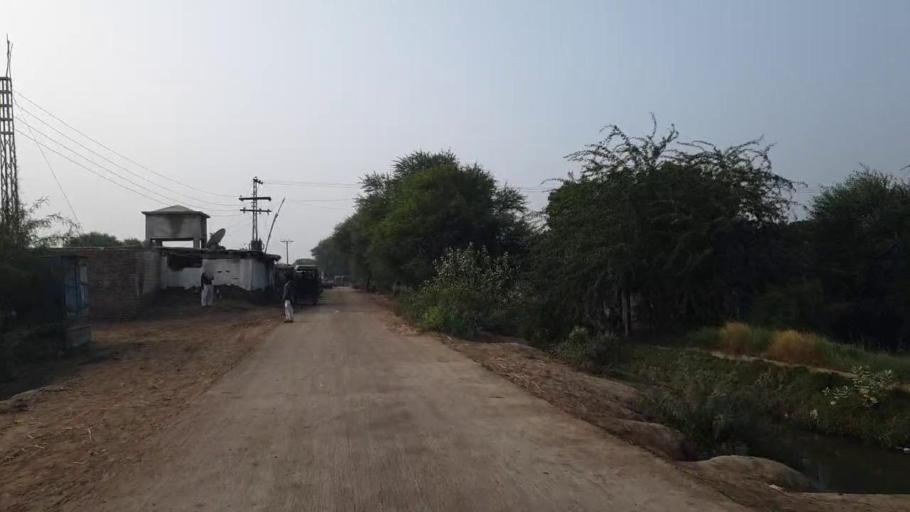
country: PK
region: Sindh
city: Tando Muhammad Khan
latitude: 25.1665
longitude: 68.6112
